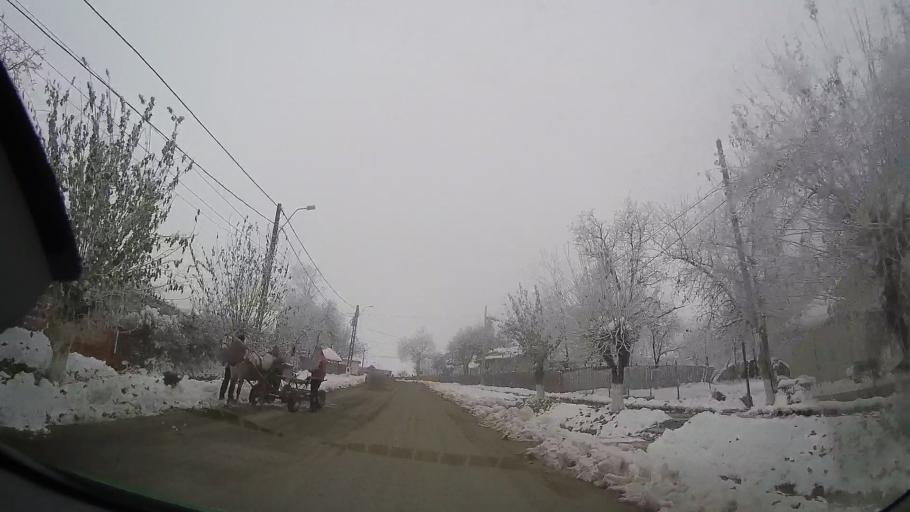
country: RO
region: Iasi
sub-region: Comuna Tansa
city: Tansa
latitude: 46.9094
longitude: 27.2296
